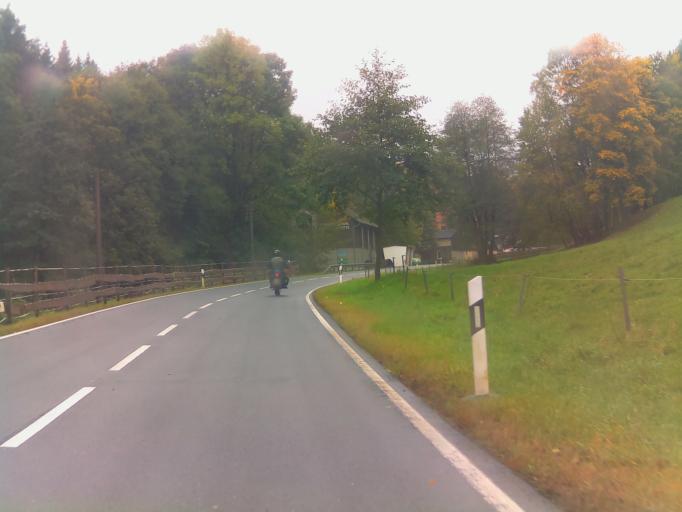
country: DE
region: Thuringia
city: Wurzbach
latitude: 50.4749
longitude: 11.5472
